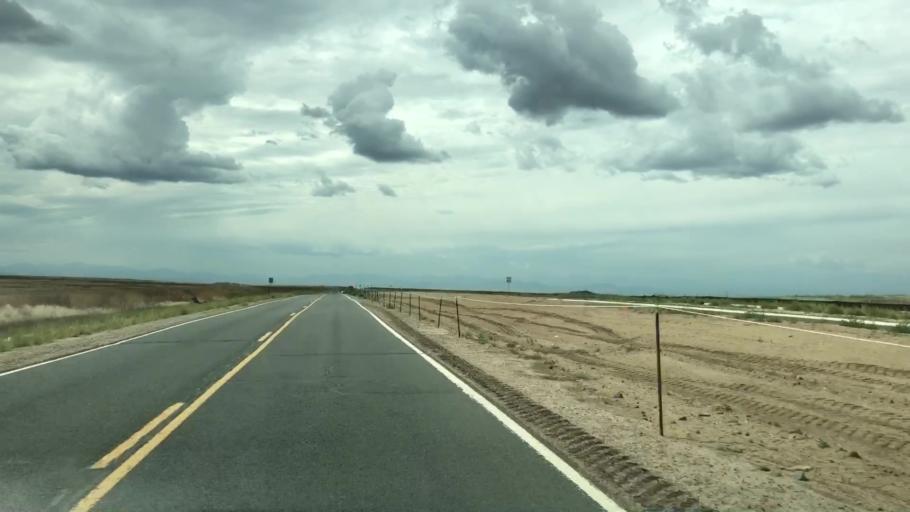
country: US
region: Colorado
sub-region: Adams County
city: Aurora
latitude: 39.7981
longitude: -104.6724
